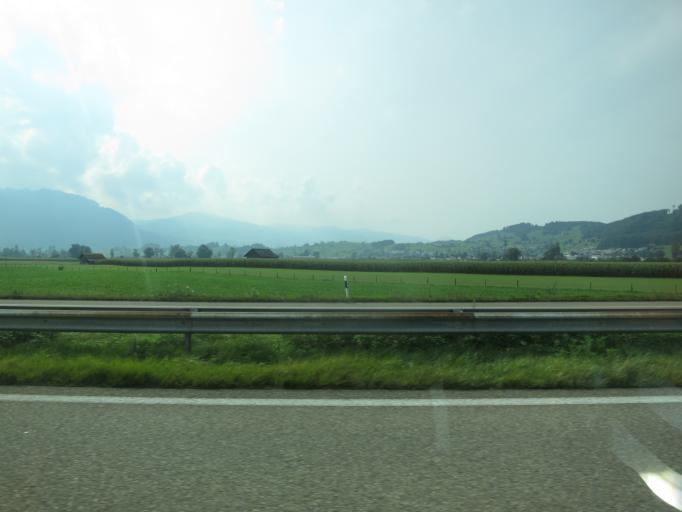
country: CH
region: Schwyz
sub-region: Bezirk March
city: Tuggen
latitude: 47.2047
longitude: 8.9657
